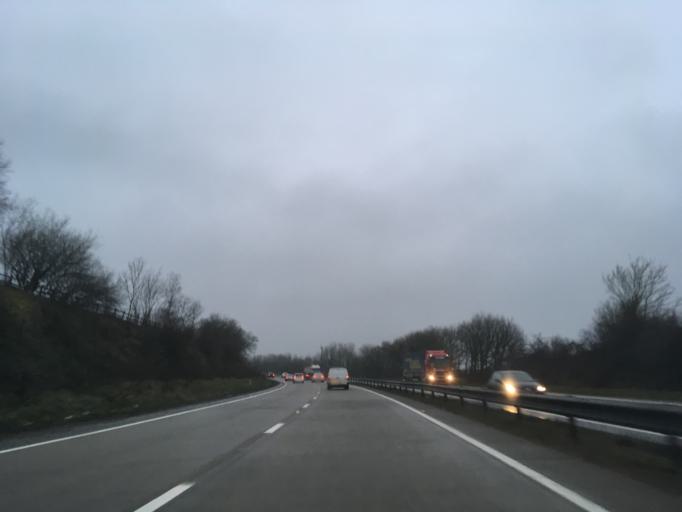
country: GB
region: Wales
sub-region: Cardiff
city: Pentyrch
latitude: 51.4989
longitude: -3.2968
